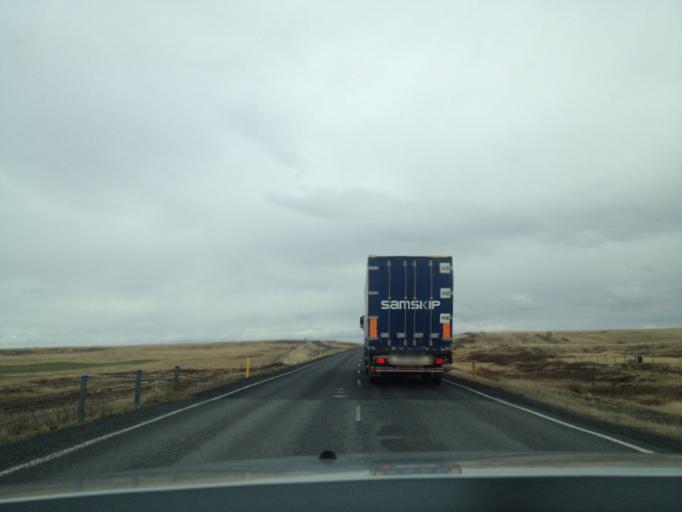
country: IS
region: South
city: Vestmannaeyjar
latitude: 63.7938
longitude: -20.3085
